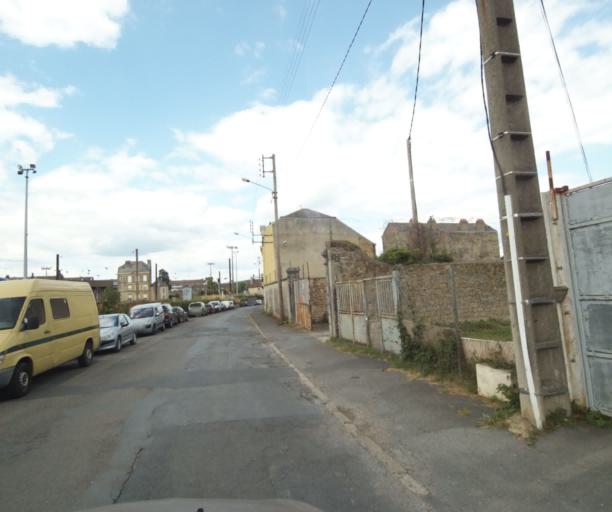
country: FR
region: Champagne-Ardenne
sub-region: Departement des Ardennes
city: Charleville-Mezieres
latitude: 49.7703
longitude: 4.7283
